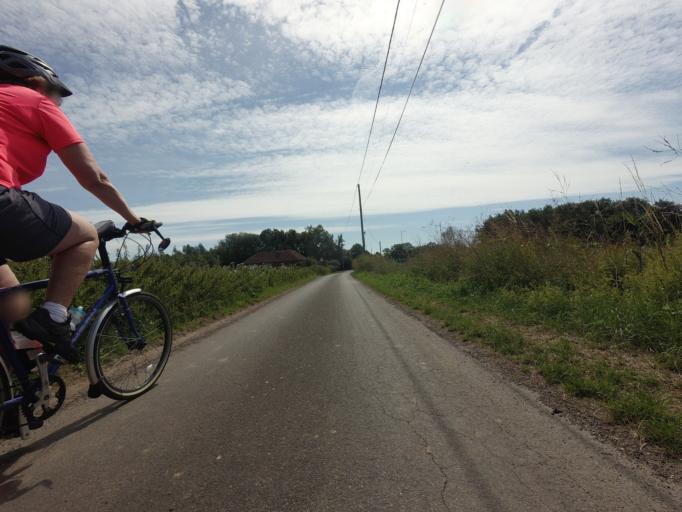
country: GB
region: England
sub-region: Kent
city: Stone
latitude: 50.9994
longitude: 0.8314
